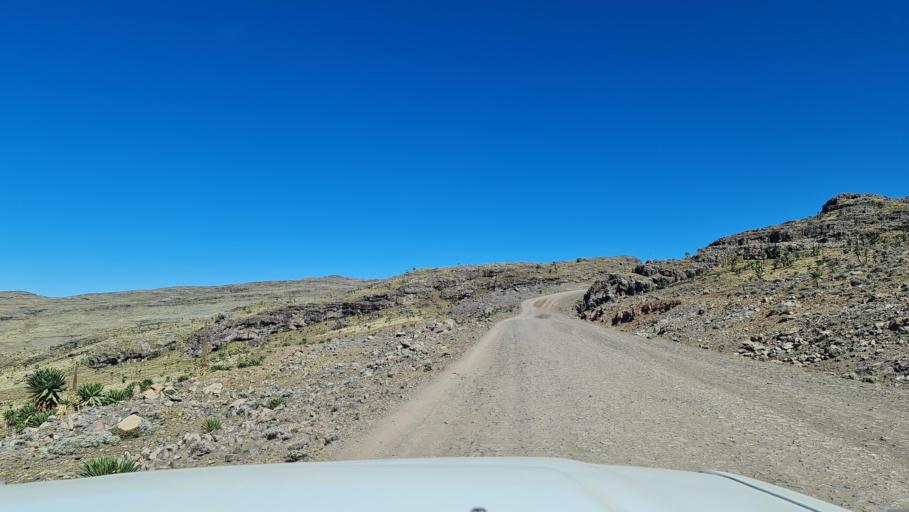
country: ET
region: Amhara
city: Debark'
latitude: 13.2205
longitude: 38.2201
